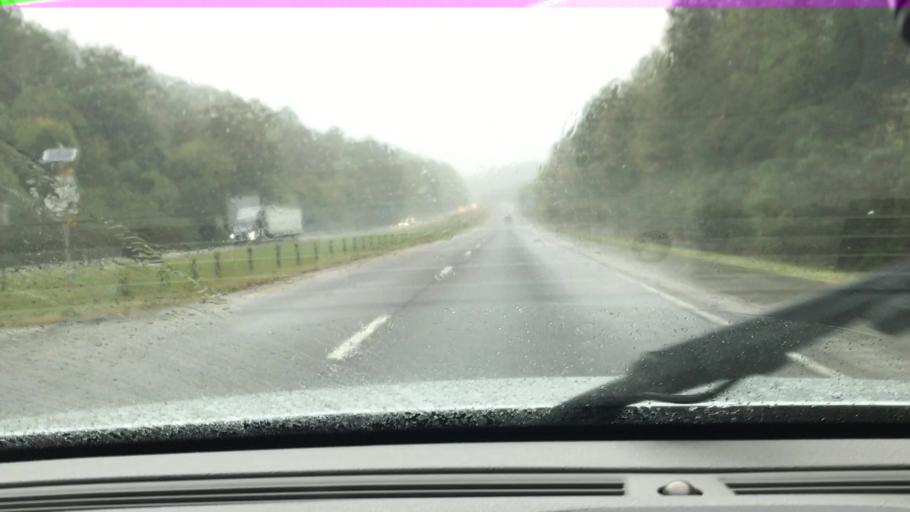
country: US
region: Alabama
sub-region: Limestone County
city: Ardmore
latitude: 34.9906
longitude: -86.8794
